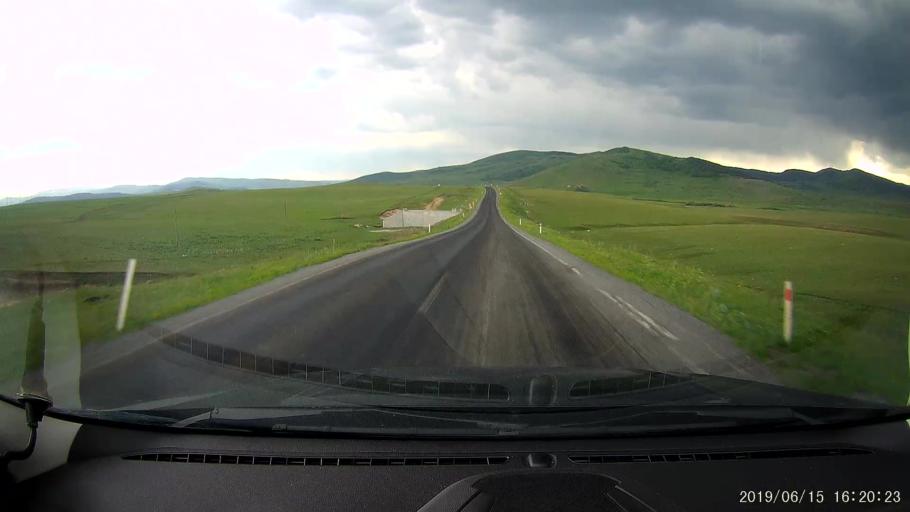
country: TR
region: Ardahan
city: Hanak
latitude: 41.2151
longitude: 42.8485
